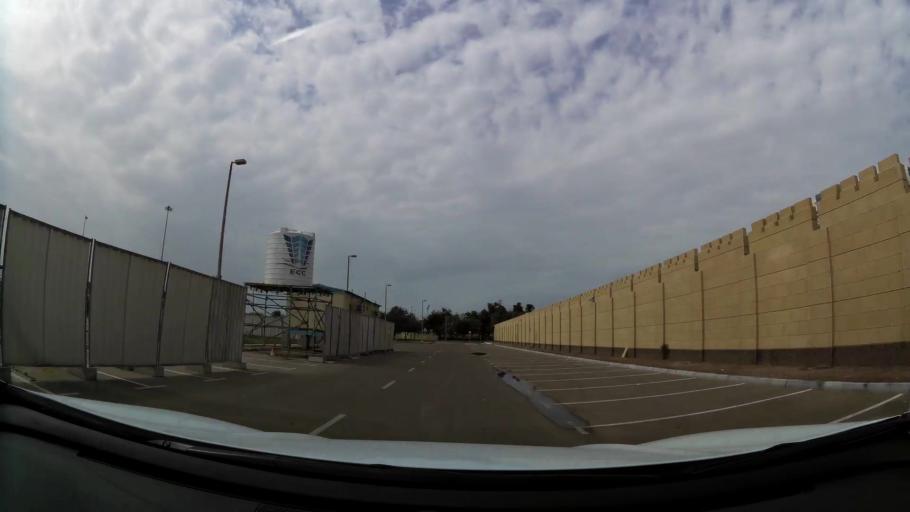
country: AE
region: Abu Dhabi
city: Abu Dhabi
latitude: 24.4102
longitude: 54.4644
